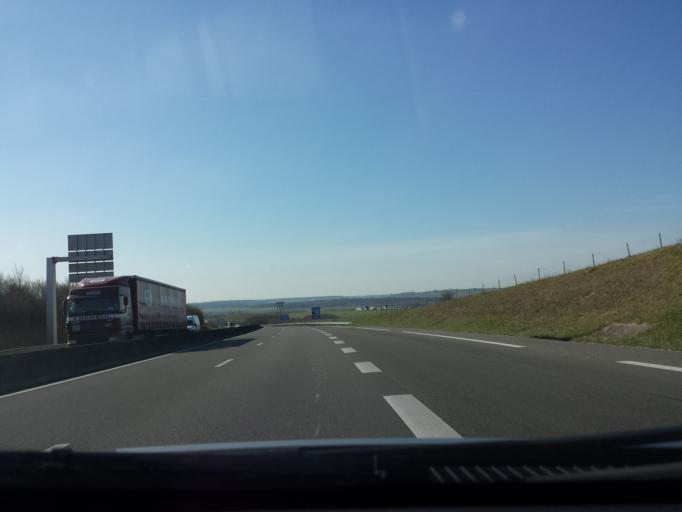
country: FR
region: Picardie
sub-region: Departement de la Somme
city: Salouel
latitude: 49.8583
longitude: 2.2640
